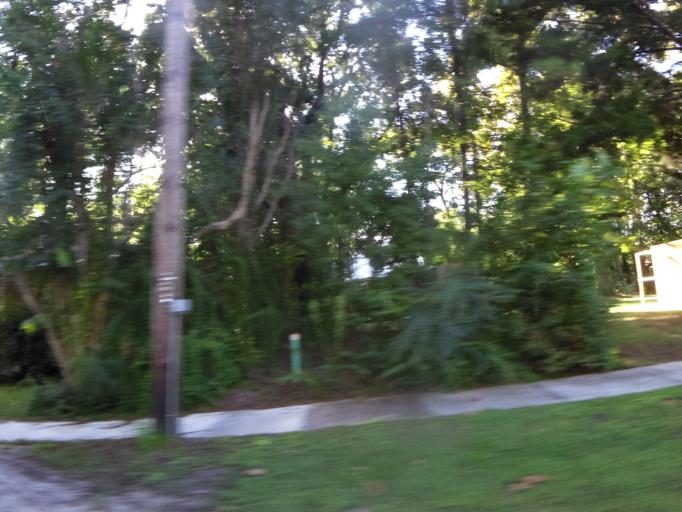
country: US
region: Florida
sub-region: Wakulla County
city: Crawfordville
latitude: 30.0608
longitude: -84.4916
